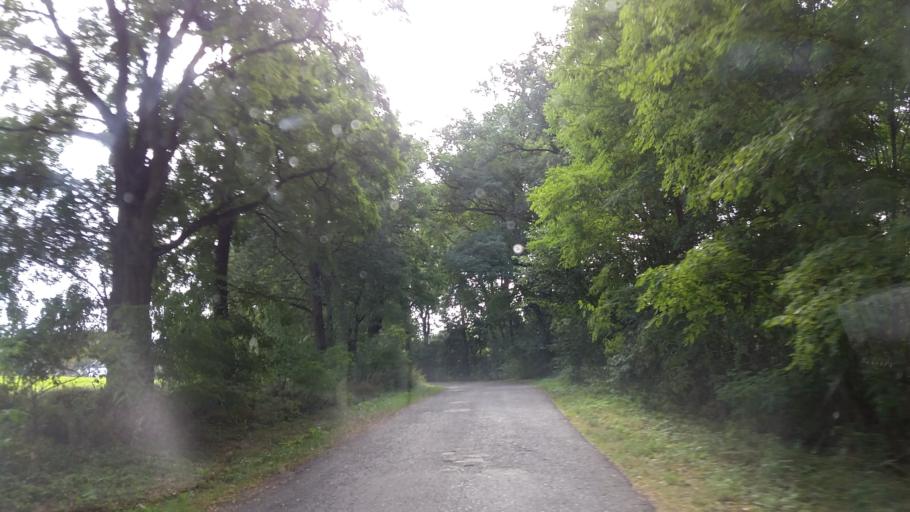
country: PL
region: West Pomeranian Voivodeship
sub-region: Powiat stargardzki
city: Suchan
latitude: 53.2312
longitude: 15.3581
